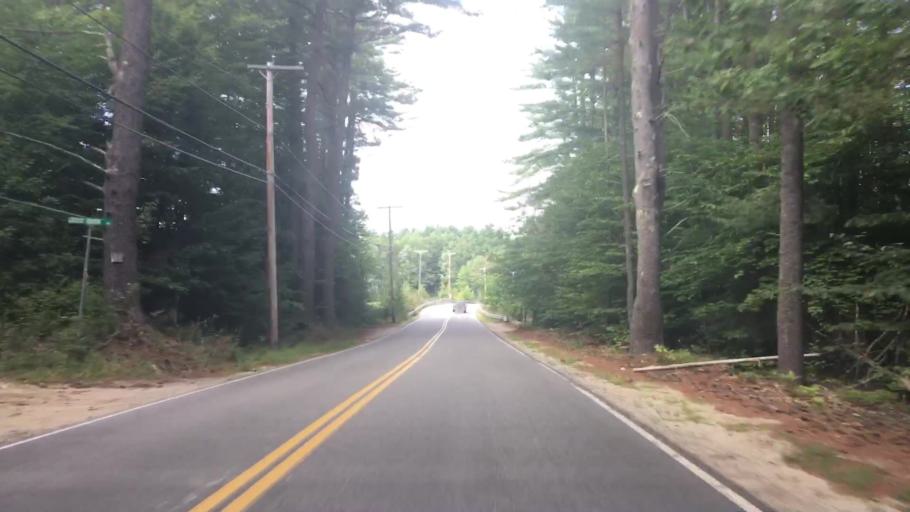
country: US
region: Maine
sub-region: Oxford County
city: Oxford
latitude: 44.1201
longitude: -70.5055
